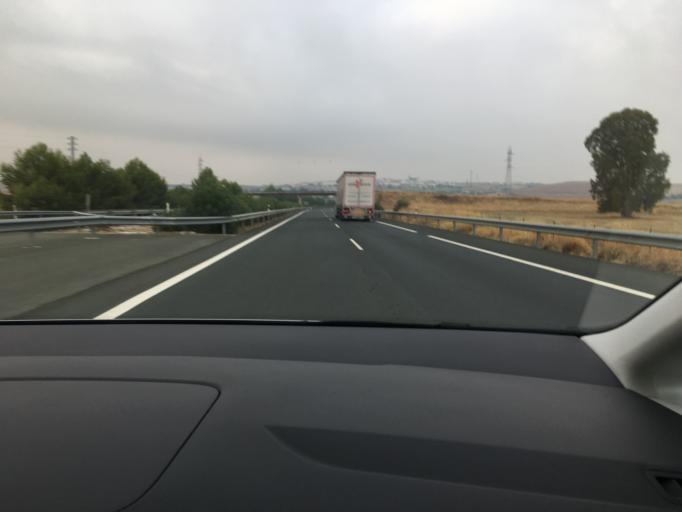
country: ES
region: Andalusia
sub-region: Province of Cordoba
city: La Carlota
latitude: 37.6877
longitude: -4.9233
